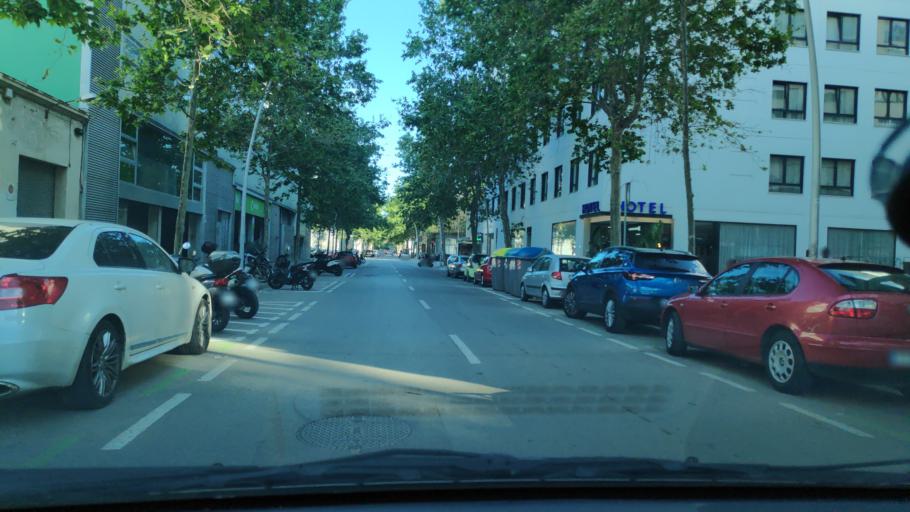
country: ES
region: Catalonia
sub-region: Provincia de Barcelona
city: Sant Marti
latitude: 41.4006
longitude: 2.1907
